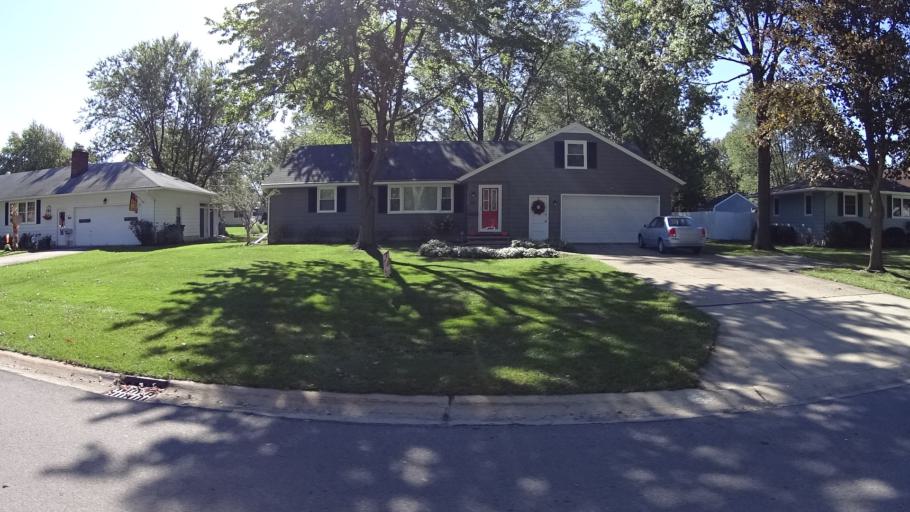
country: US
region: Ohio
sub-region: Lorain County
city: Amherst
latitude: 41.4088
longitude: -82.2242
